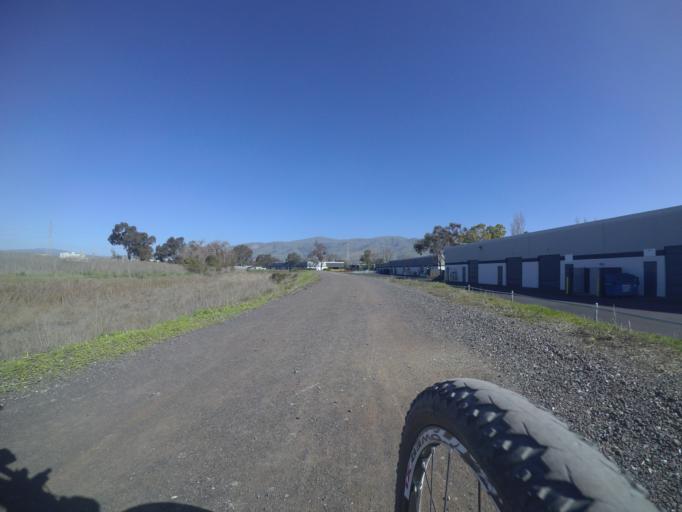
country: US
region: California
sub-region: Santa Clara County
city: Milpitas
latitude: 37.4795
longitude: -121.9491
